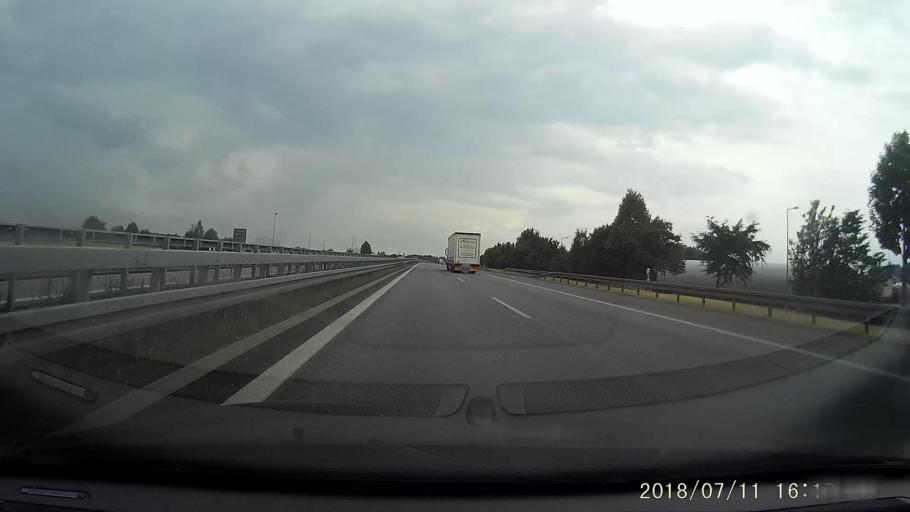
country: DE
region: Saxony
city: Goerlitz
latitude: 51.1863
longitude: 14.9979
